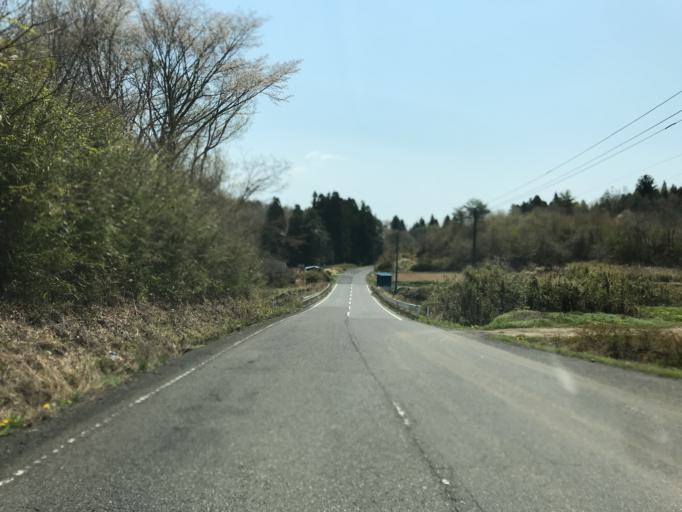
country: JP
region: Fukushima
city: Ishikawa
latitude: 37.1024
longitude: 140.4045
